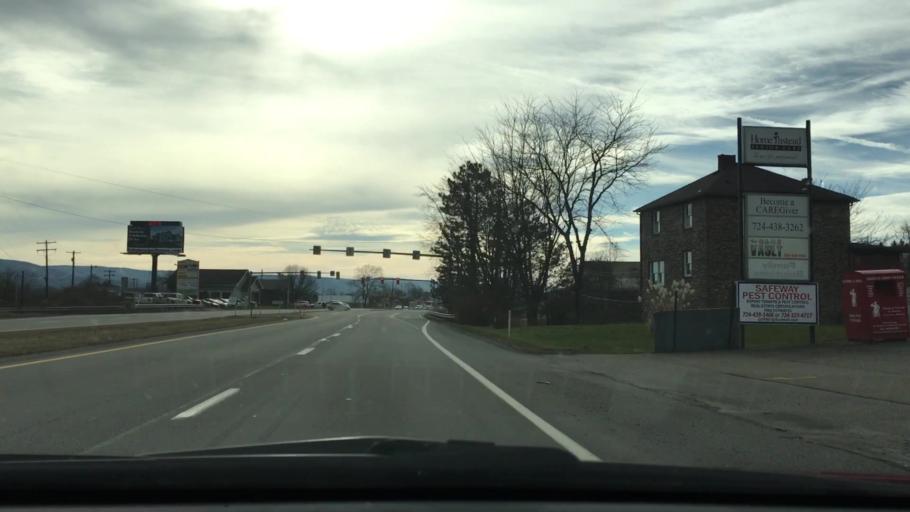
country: US
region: Pennsylvania
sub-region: Fayette County
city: Oliver
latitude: 39.9276
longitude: -79.7275
